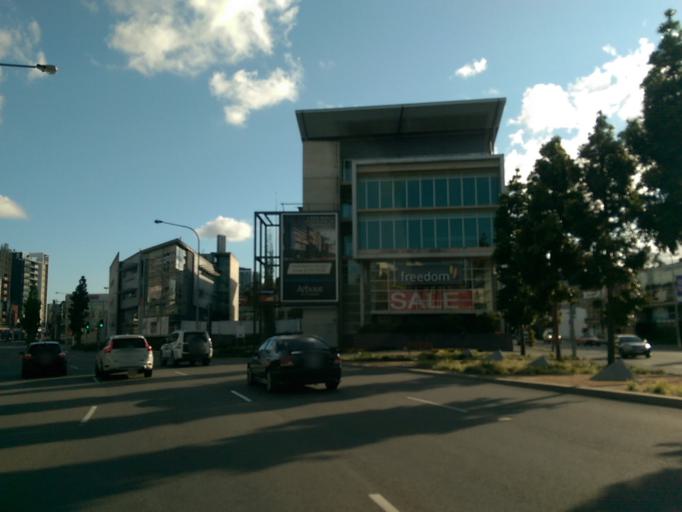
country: AU
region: Queensland
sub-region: Brisbane
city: Fortitude Valley
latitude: -27.4503
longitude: 153.0414
